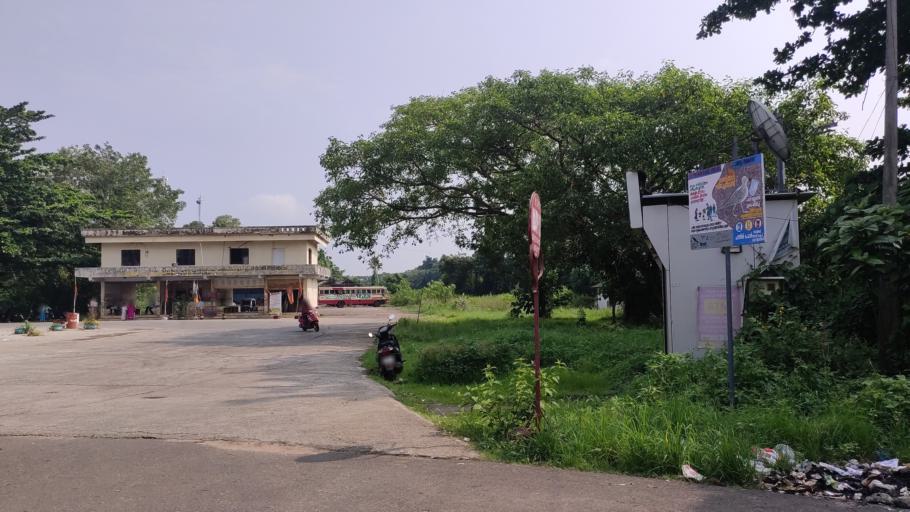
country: IN
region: Kerala
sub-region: Pattanamtitta
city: Adur
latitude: 9.2251
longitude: 76.6748
